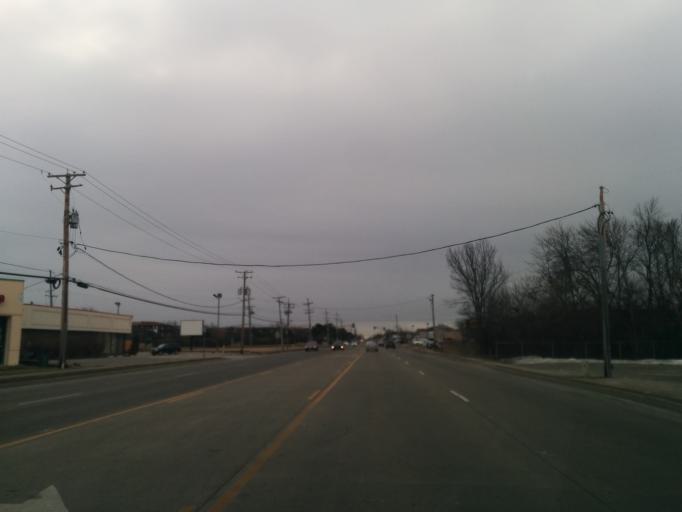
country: US
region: Illinois
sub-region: Cook County
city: Northbrook
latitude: 42.0918
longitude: -87.8750
